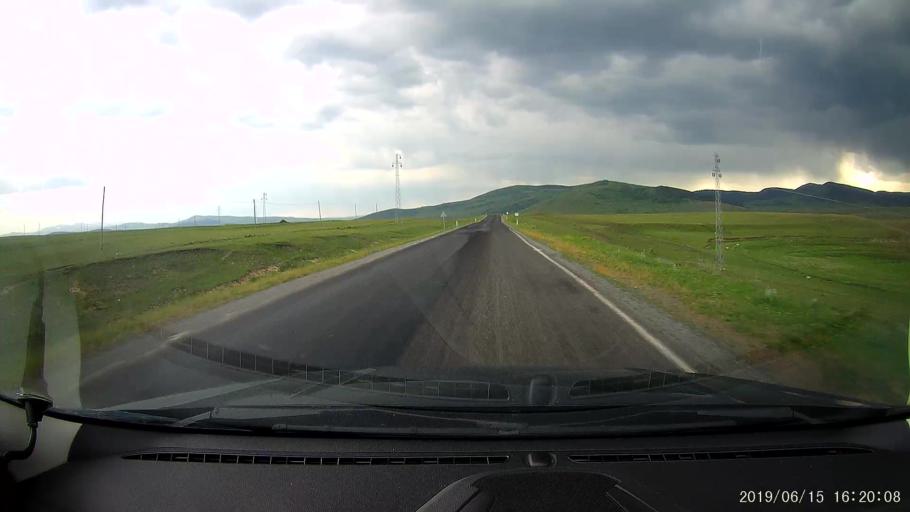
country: TR
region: Ardahan
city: Hanak
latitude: 41.2184
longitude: 42.8489
